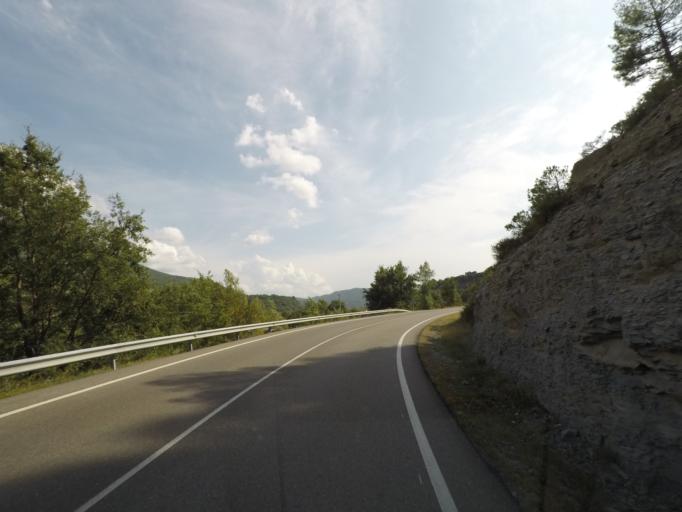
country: ES
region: Aragon
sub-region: Provincia de Huesca
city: Laspuna
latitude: 42.5089
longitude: 0.1449
